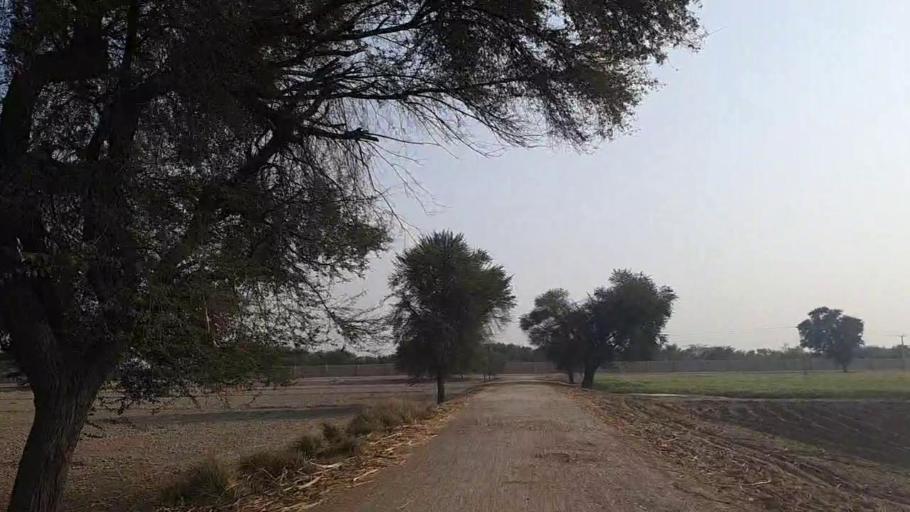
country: PK
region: Sindh
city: Sann
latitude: 26.1108
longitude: 68.1724
